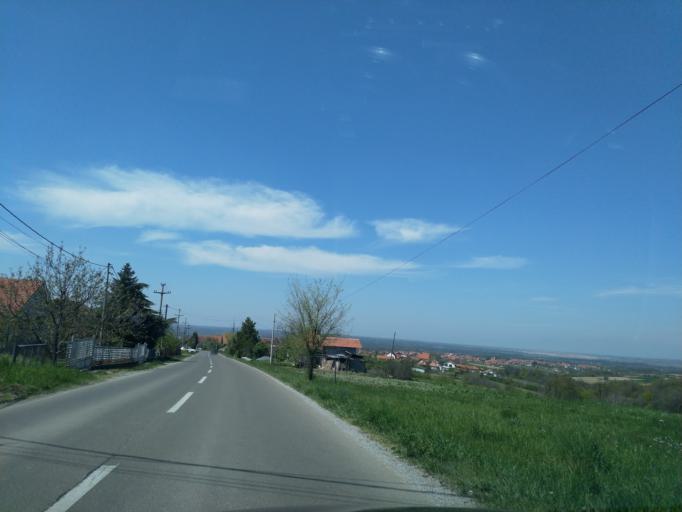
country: RS
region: Central Serbia
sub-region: Belgrade
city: Lazarevac
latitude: 44.3736
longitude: 20.2979
